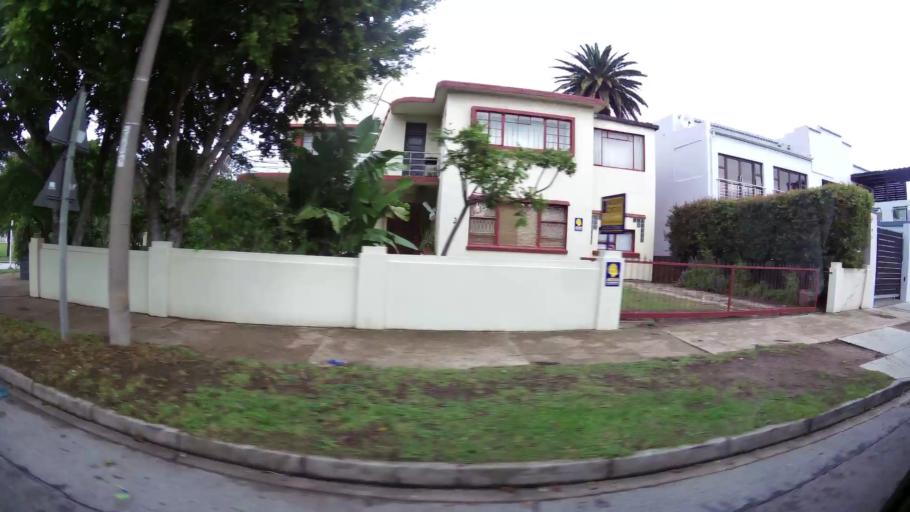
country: ZA
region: Eastern Cape
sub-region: Nelson Mandela Bay Metropolitan Municipality
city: Port Elizabeth
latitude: -33.9572
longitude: 25.5971
